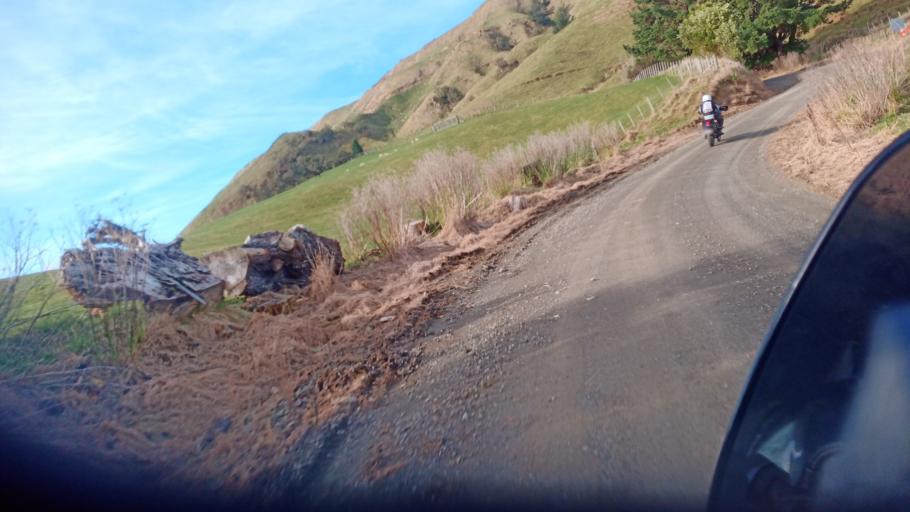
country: NZ
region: Bay of Plenty
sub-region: Opotiki District
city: Opotiki
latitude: -38.4461
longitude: 177.5387
